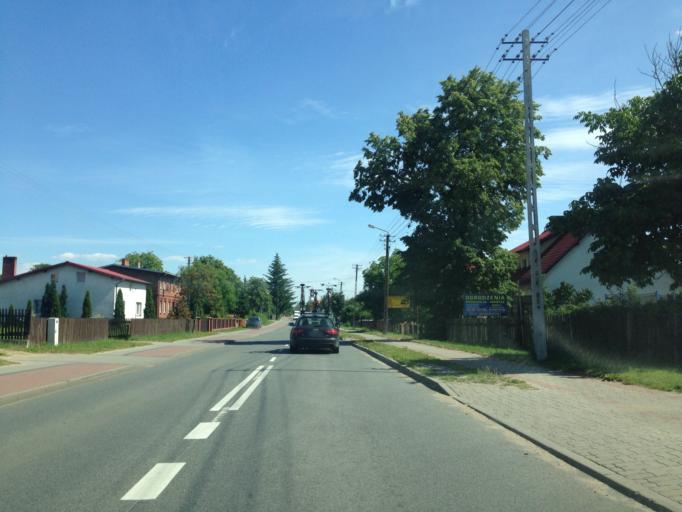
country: PL
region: Kujawsko-Pomorskie
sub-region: Powiat swiecki
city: Osie
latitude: 53.6030
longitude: 18.3354
